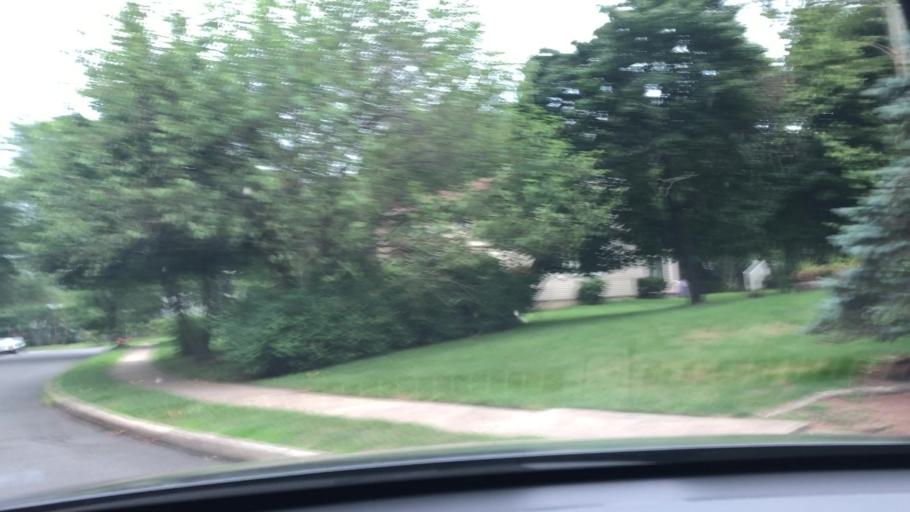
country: US
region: New Jersey
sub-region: Middlesex County
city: East Brunswick
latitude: 40.4187
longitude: -74.4257
